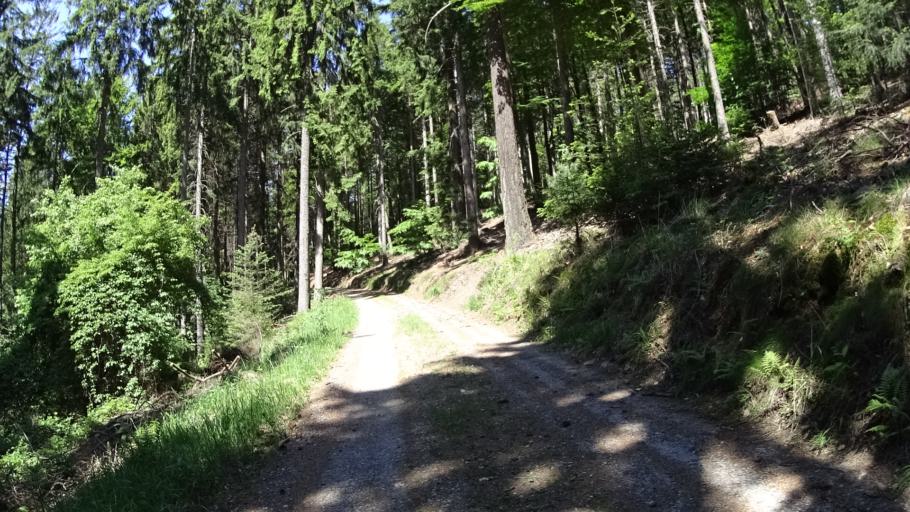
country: DE
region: Baden-Wuerttemberg
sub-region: Karlsruhe Region
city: Neckargemund
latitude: 49.4165
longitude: 8.7825
